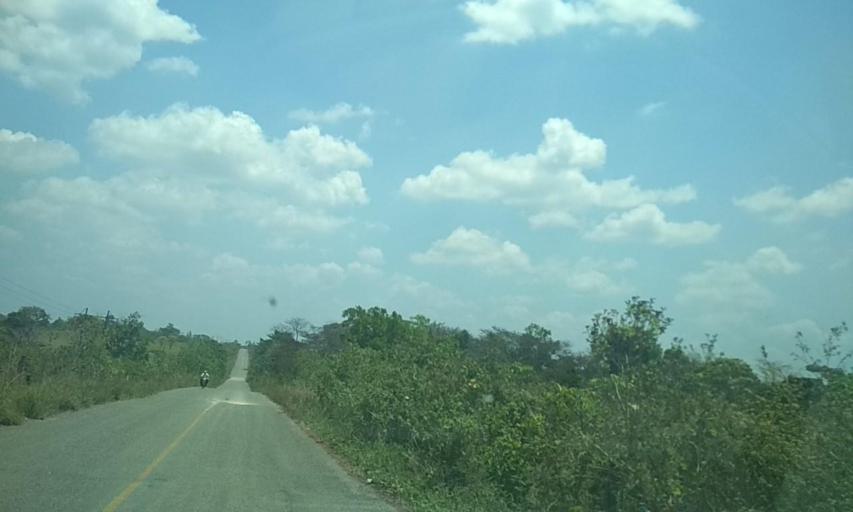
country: MX
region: Tabasco
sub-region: Huimanguillo
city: Francisco Rueda
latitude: 17.8216
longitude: -93.8715
